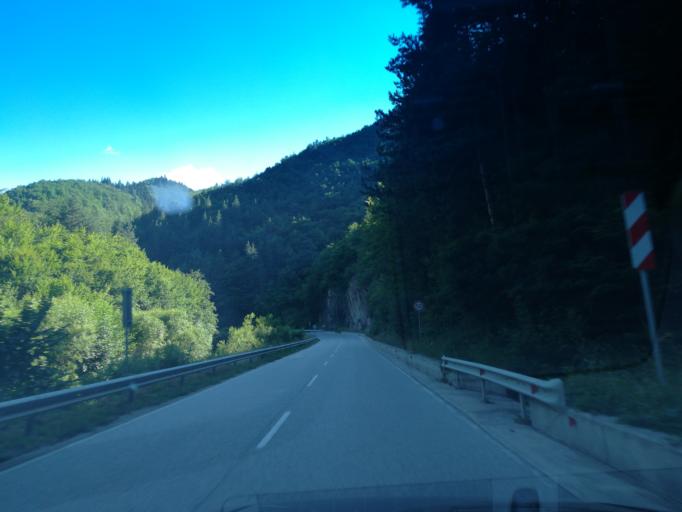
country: BG
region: Smolyan
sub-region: Obshtina Chepelare
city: Chepelare
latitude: 41.7921
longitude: 24.7095
